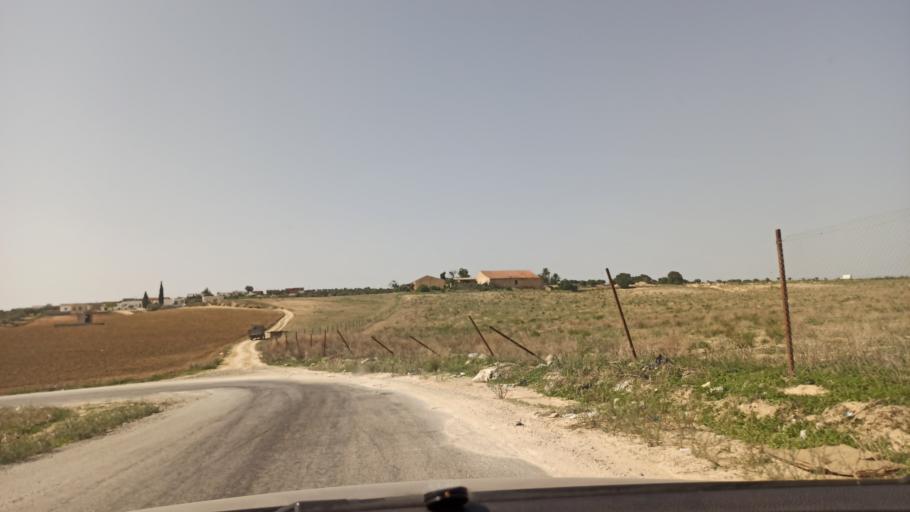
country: TN
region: Manouba
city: Manouba
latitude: 36.7326
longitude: 10.0935
